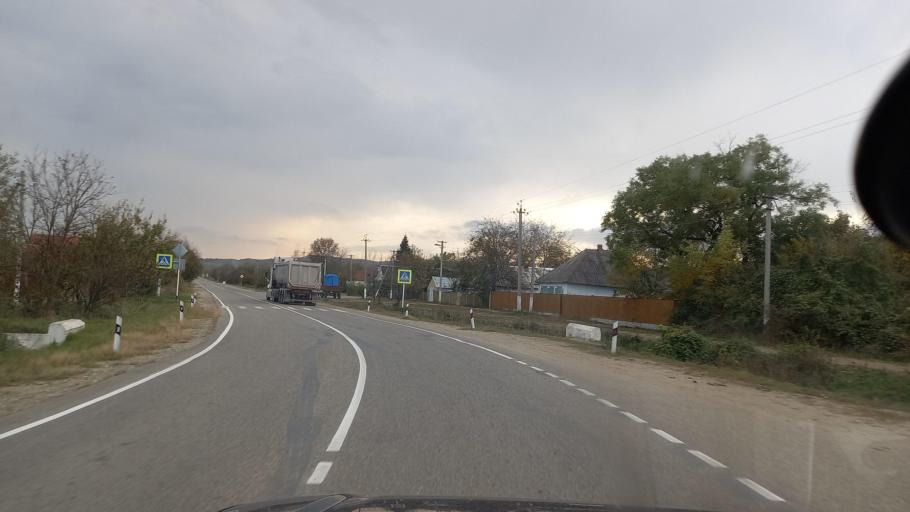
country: RU
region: Krasnodarskiy
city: Mostovskoy
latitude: 44.3883
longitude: 40.7399
